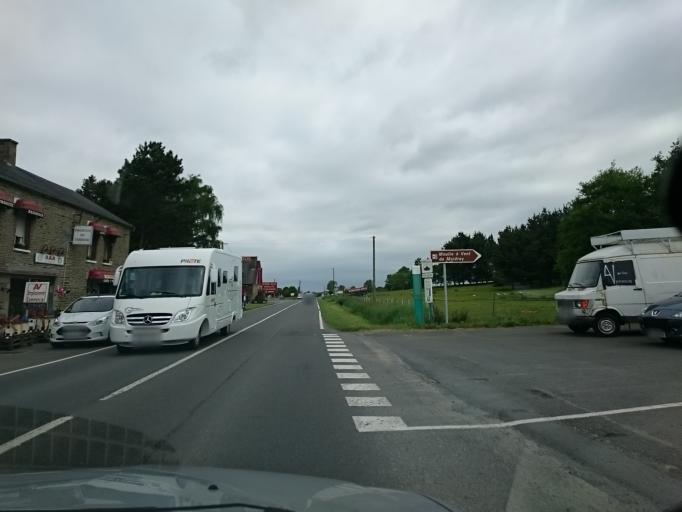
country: FR
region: Lower Normandy
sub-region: Departement de la Manche
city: Pontorson
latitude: 48.5812
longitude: -1.5118
